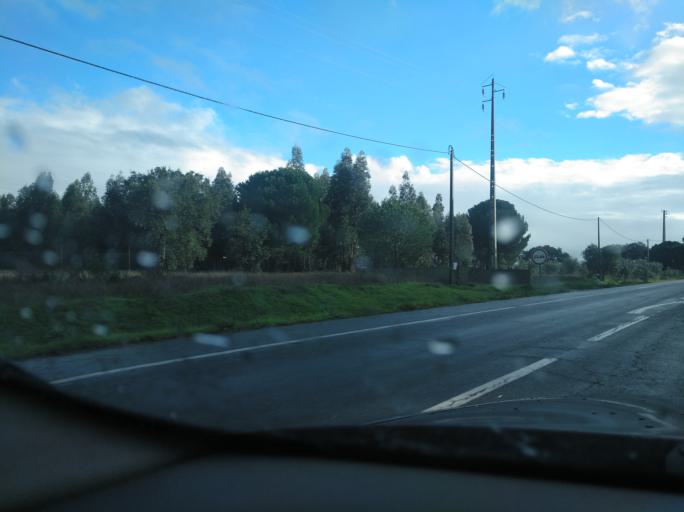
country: PT
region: Setubal
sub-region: Grandola
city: Grandola
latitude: 38.0359
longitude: -8.4006
